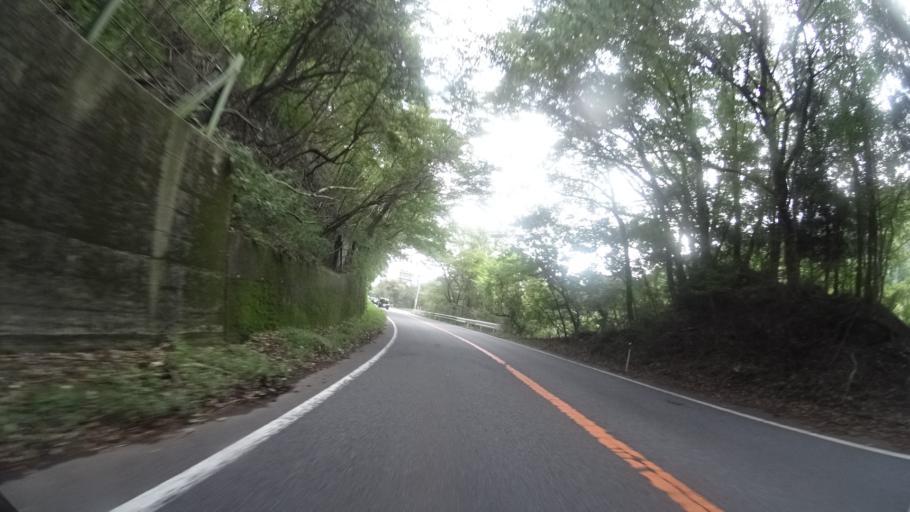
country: JP
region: Oita
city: Beppu
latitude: 33.2709
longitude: 131.4165
